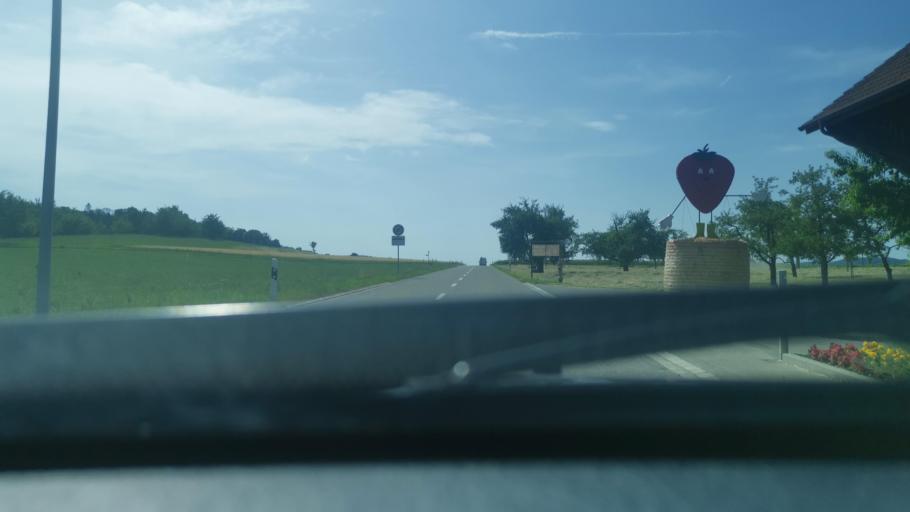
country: CH
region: Zurich
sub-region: Bezirk Winterthur
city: Sulz
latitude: 47.5690
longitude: 8.7998
